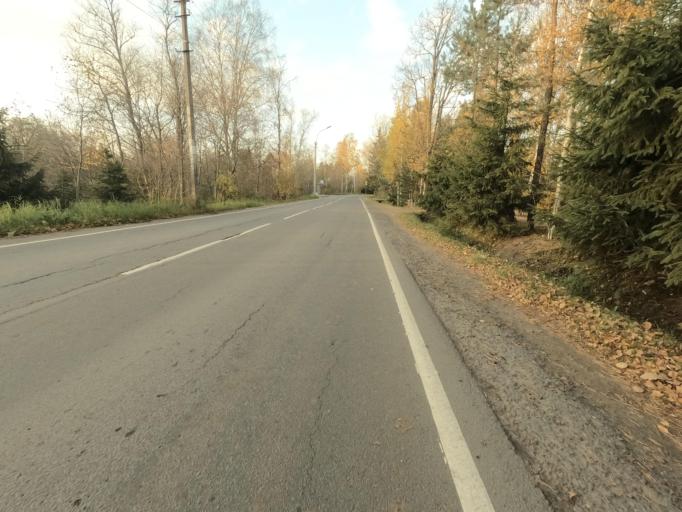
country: RU
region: St.-Petersburg
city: Beloostrov
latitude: 60.1594
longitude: 30.0061
